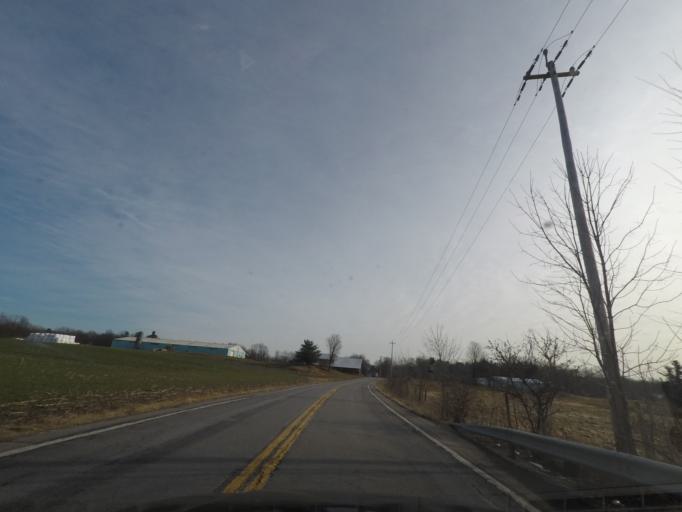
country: US
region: New York
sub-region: Saratoga County
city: Stillwater
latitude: 42.9878
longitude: -73.6887
